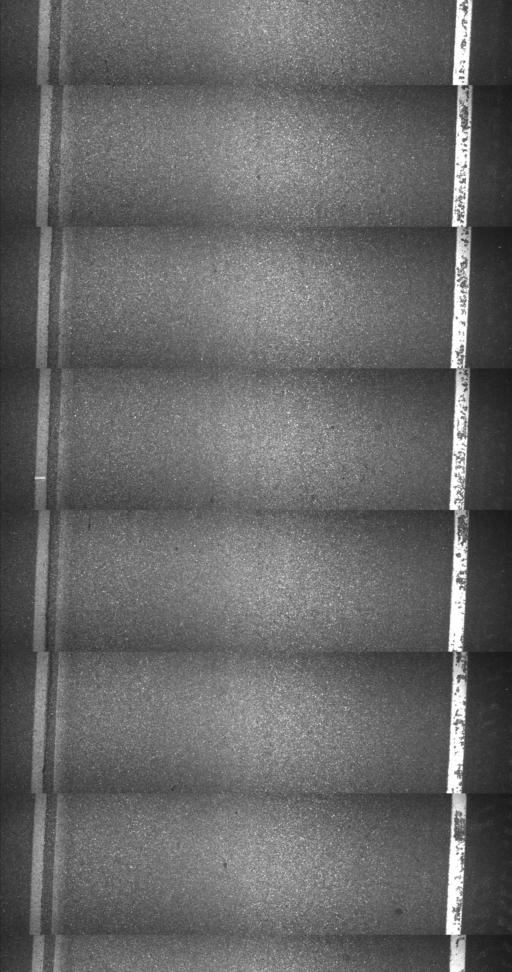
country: US
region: Vermont
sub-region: Caledonia County
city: Lyndonville
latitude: 44.8066
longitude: -71.8511
